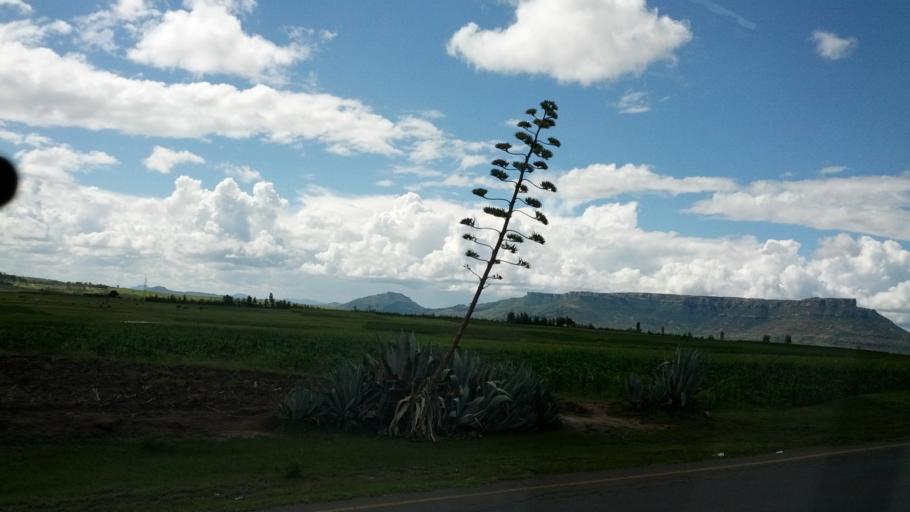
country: LS
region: Mafeteng
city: Mafeteng
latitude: -29.6847
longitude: 27.4437
